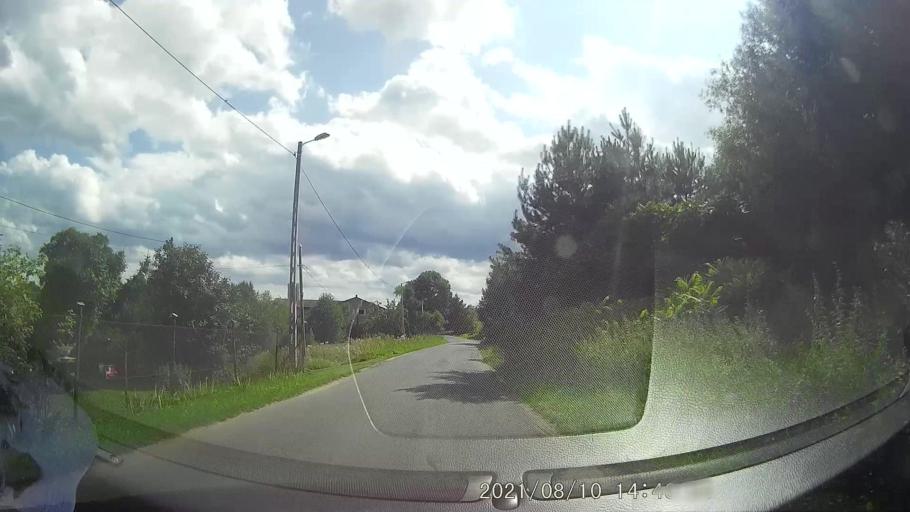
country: PL
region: Lower Silesian Voivodeship
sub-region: Powiat klodzki
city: Radkow
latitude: 50.5297
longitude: 16.4128
